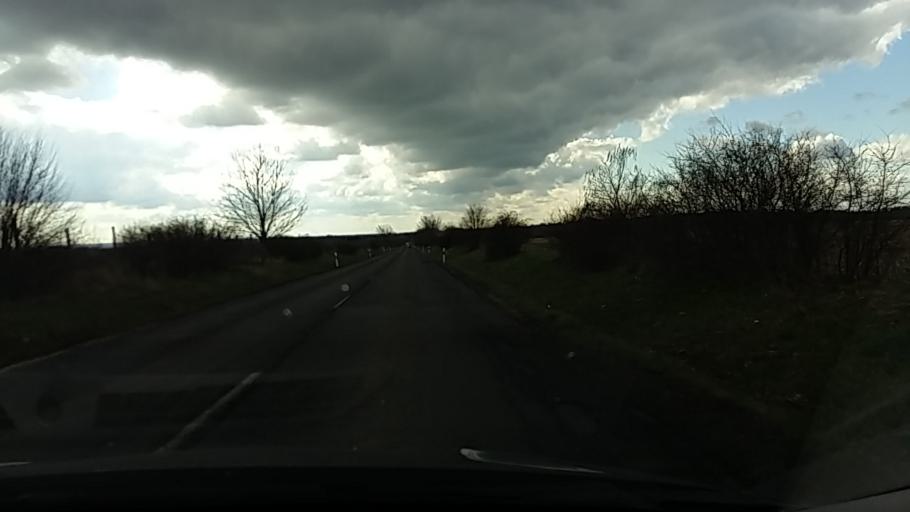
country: HU
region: Somogy
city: Bohonye
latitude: 46.4317
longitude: 17.3782
